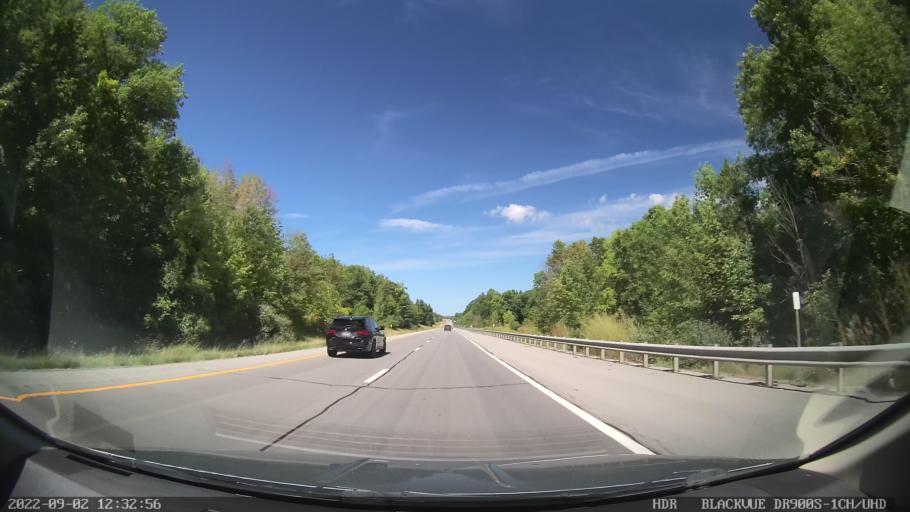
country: US
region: New York
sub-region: Livingston County
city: Dansville
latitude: 42.6300
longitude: -77.7799
